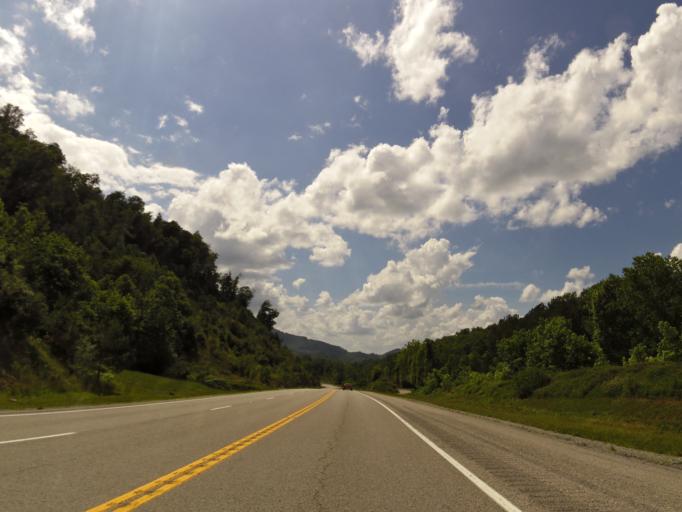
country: US
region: Kentucky
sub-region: Harlan County
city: Harlan
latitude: 36.7786
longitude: -83.2153
